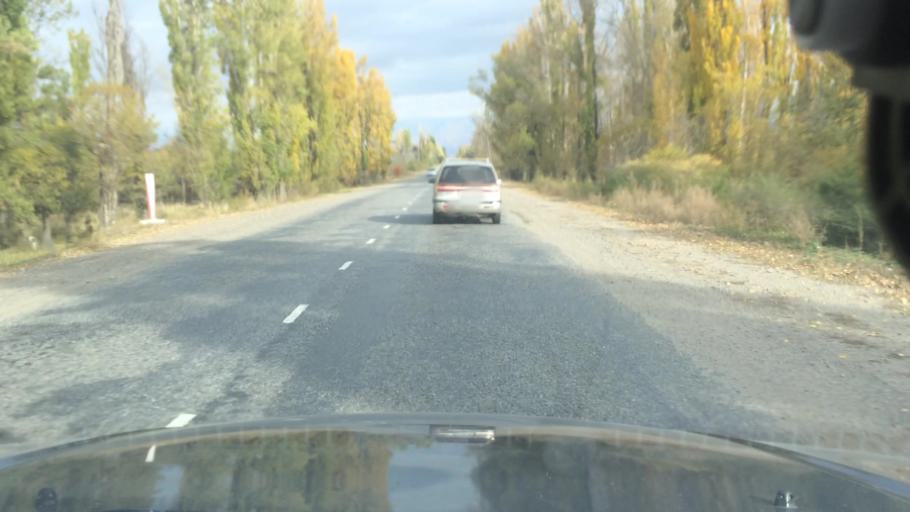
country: KG
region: Ysyk-Koel
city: Tyup
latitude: 42.6156
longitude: 78.3654
